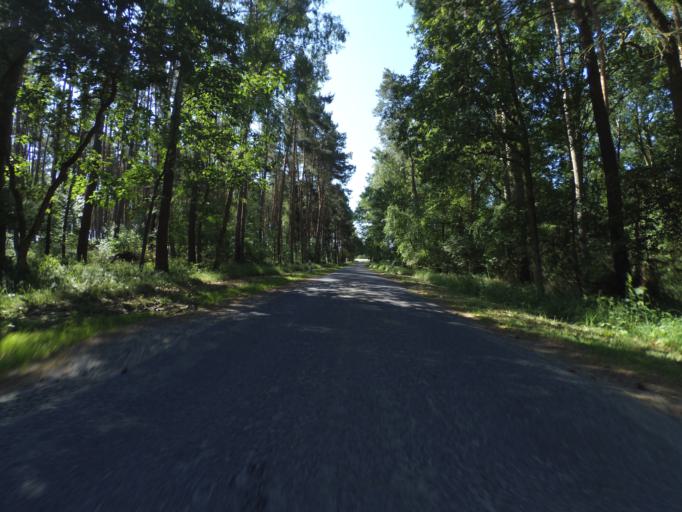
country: DE
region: Brandenburg
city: Putlitz
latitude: 53.1962
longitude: 12.0351
